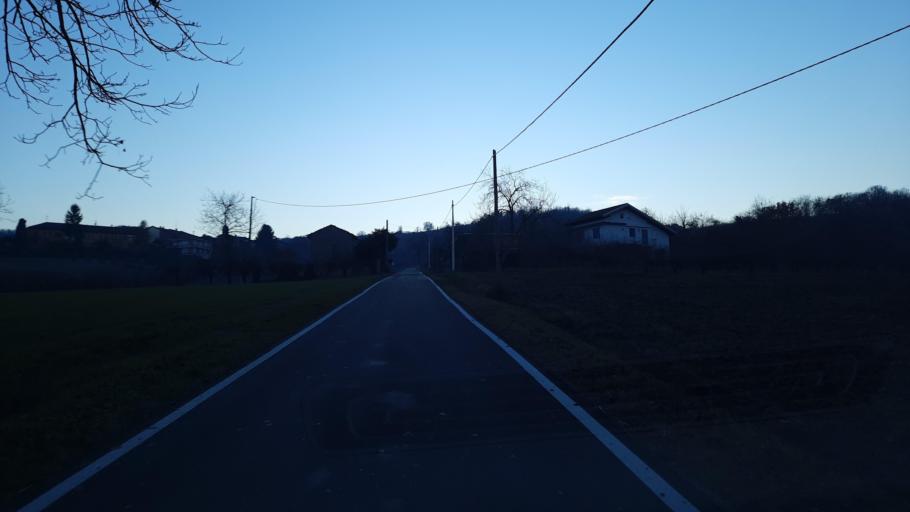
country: IT
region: Piedmont
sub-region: Provincia di Alessandria
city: Mombello Monferrato
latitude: 45.1547
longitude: 8.2572
